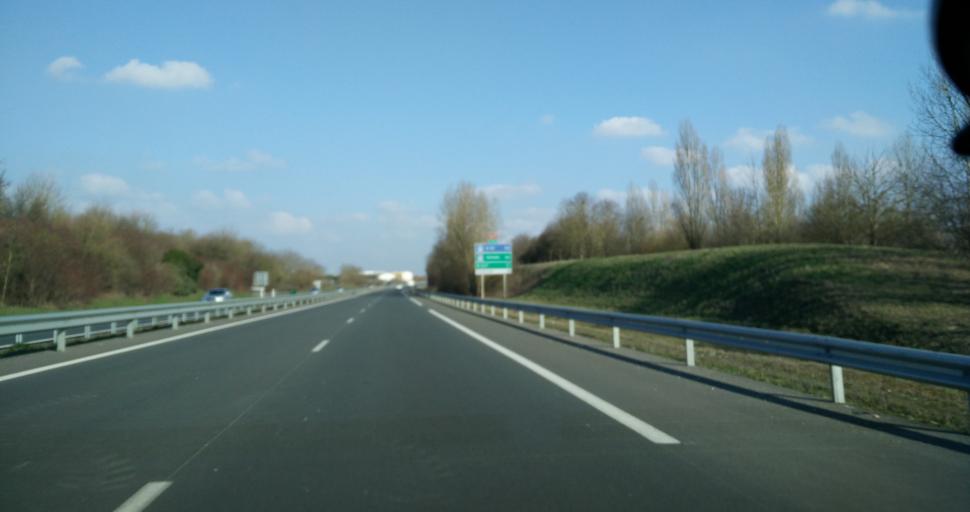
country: FR
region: Poitou-Charentes
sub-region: Departement de la Charente-Maritime
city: Sainte-Soulle
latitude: 46.2042
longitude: -1.0204
